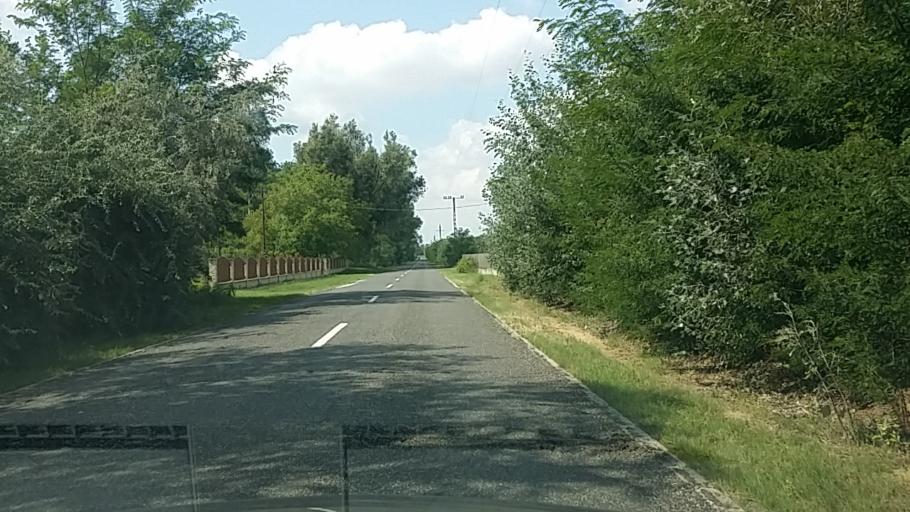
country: HU
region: Bacs-Kiskun
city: Lakitelek
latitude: 46.8612
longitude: 19.9736
